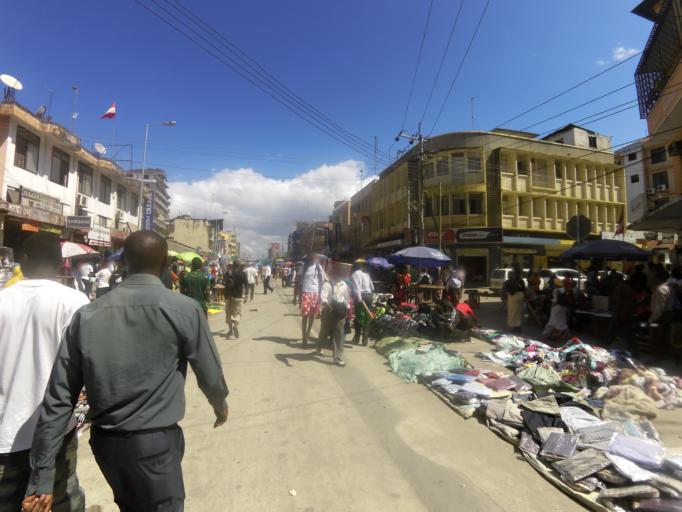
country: TZ
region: Dar es Salaam
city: Dar es Salaam
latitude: -6.8221
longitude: 39.2732
